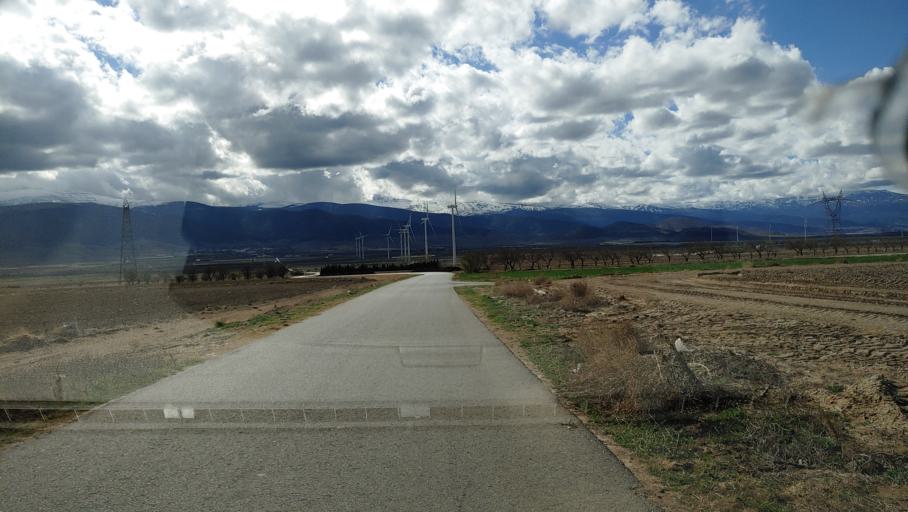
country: ES
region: Andalusia
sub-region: Provincia de Granada
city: Hueneja
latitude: 37.2245
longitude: -2.9658
